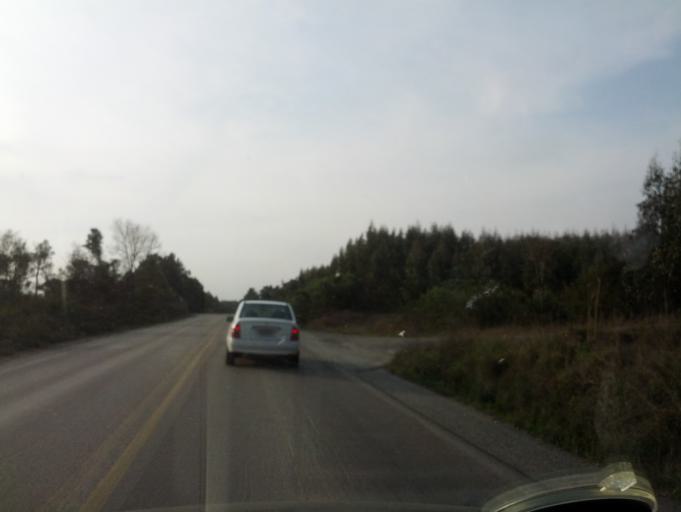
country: BR
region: Santa Catarina
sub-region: Otacilio Costa
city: Otacilio Costa
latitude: -27.4503
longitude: -50.1237
